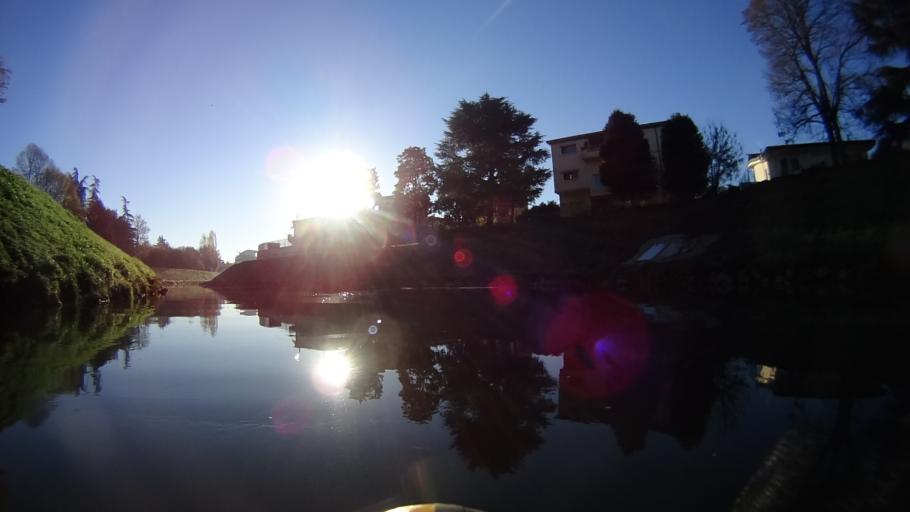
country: IT
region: Veneto
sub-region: Provincia di Vicenza
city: Vicenza
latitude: 45.5580
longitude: 11.5300
